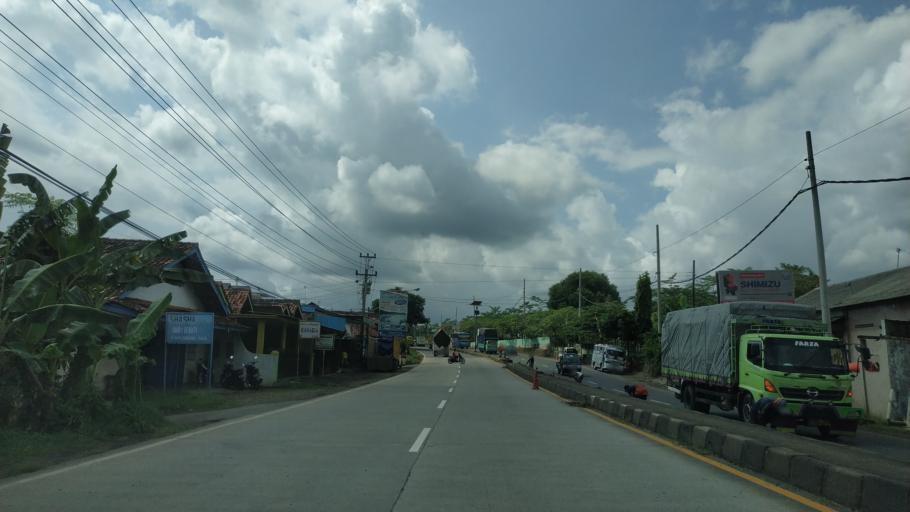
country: ID
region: Central Java
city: Pekalongan
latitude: -6.9452
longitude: 109.8108
